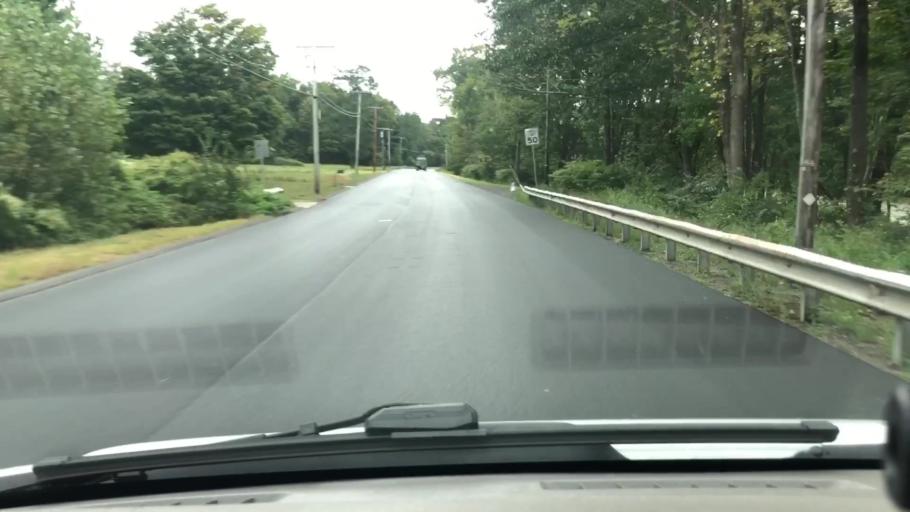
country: US
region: Massachusetts
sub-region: Franklin County
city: Buckland
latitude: 42.6172
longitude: -72.8133
